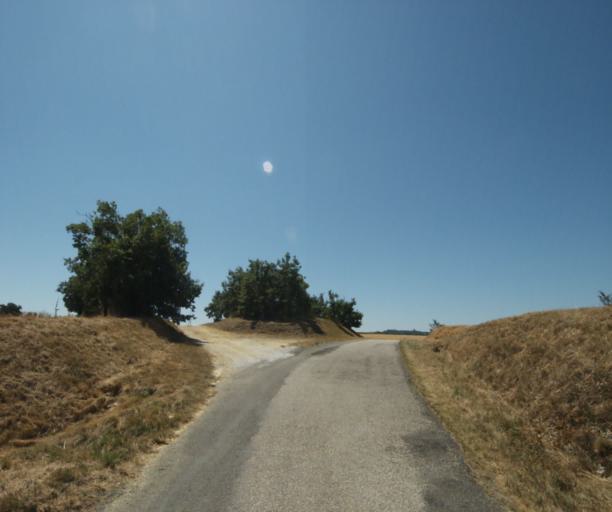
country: FR
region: Midi-Pyrenees
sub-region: Departement de la Haute-Garonne
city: Saint-Felix-Lauragais
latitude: 43.4743
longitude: 1.9176
